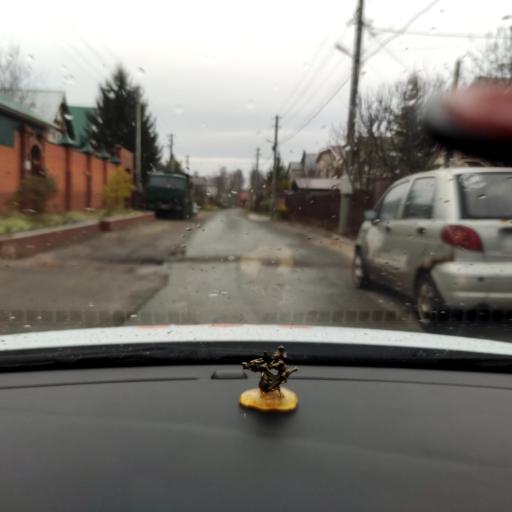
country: RU
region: Tatarstan
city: Vysokaya Gora
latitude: 55.8438
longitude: 49.2390
